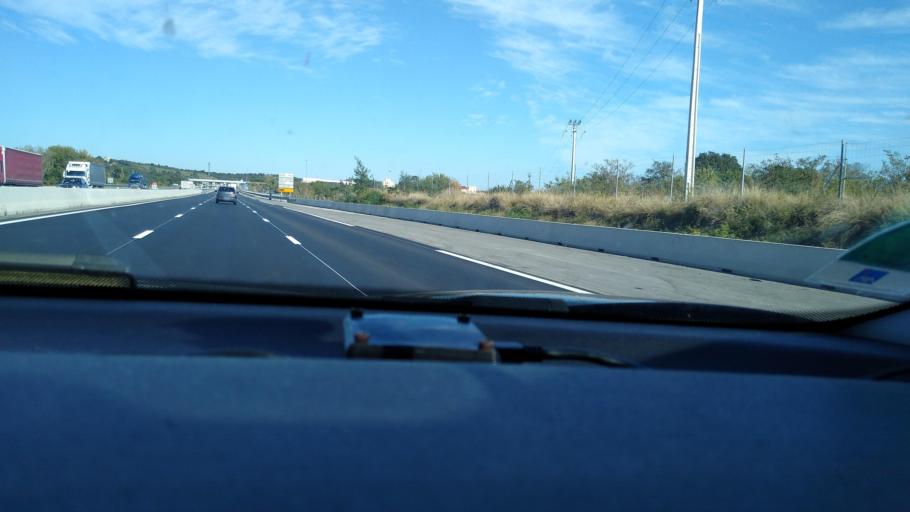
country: FR
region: Languedoc-Roussillon
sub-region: Departement des Pyrenees-Orientales
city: el Volo
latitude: 42.5145
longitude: 2.8187
